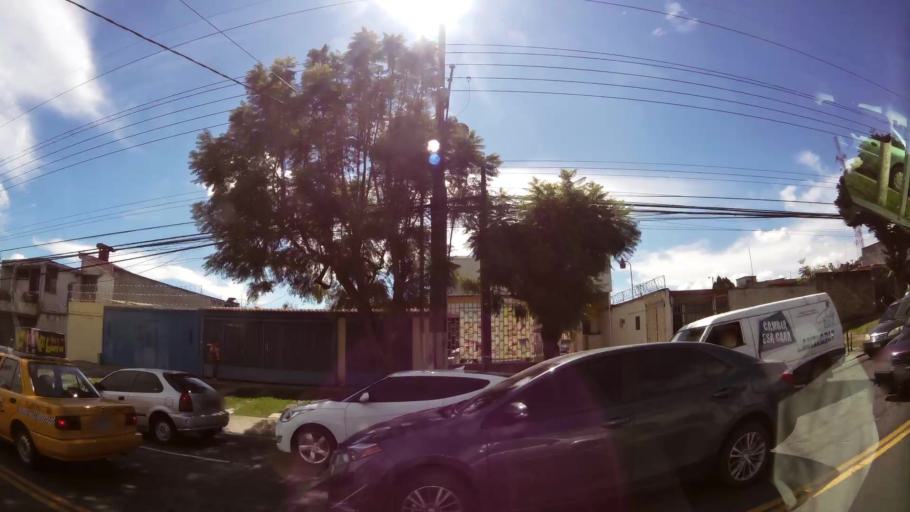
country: GT
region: Guatemala
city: Guatemala City
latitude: 14.6301
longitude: -90.5579
